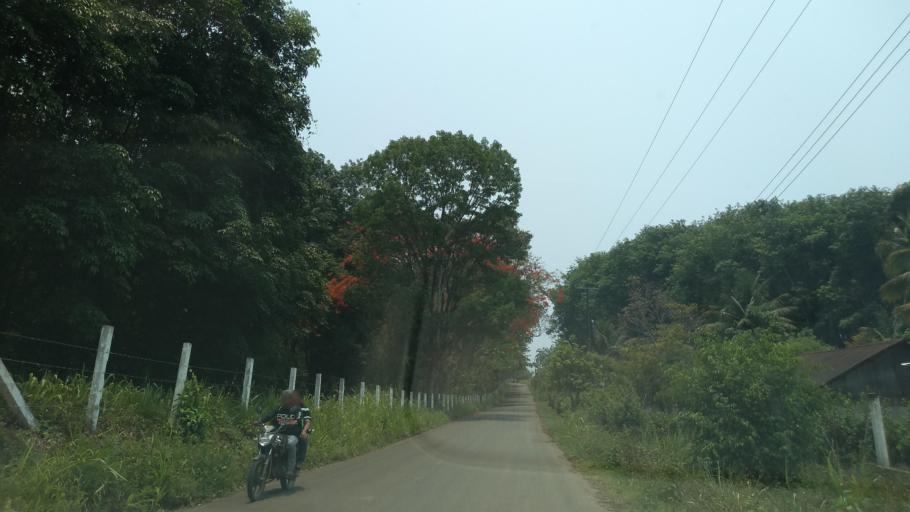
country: MX
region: Veracruz
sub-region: Tezonapa
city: Laguna Chica (Pueblo Nuevo)
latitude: 18.5133
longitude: -96.7610
